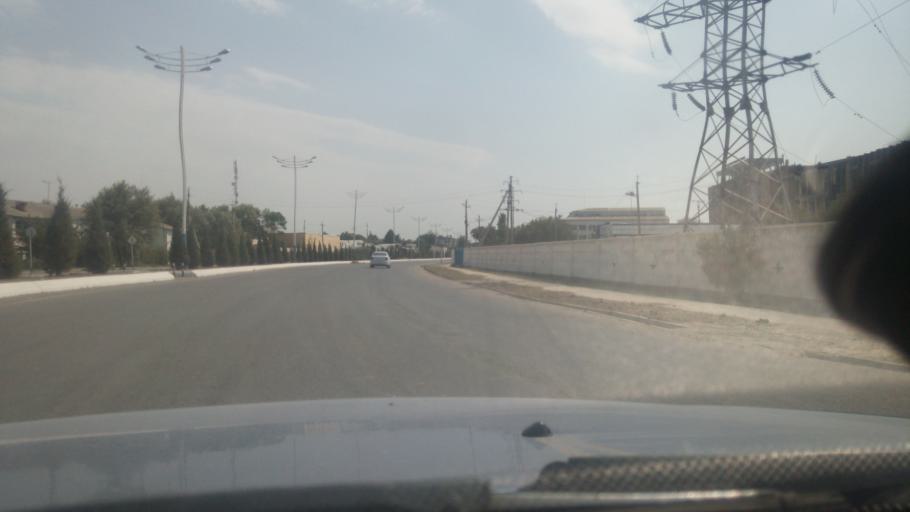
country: UZ
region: Sirdaryo
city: Guliston
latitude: 40.5205
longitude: 68.7675
